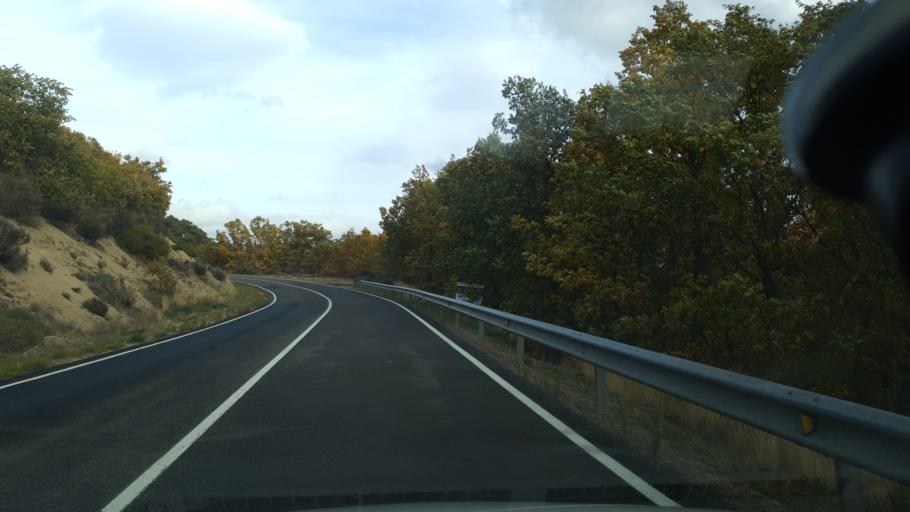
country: ES
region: Castille and Leon
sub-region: Provincia de Avila
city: Hoyocasero
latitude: 40.3903
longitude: -4.9974
